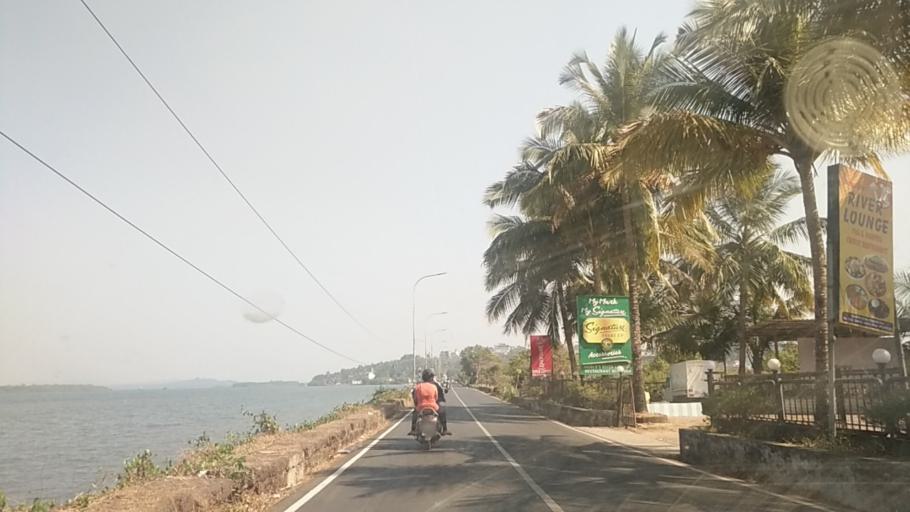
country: IN
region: Goa
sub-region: North Goa
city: Panaji
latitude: 15.5025
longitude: 73.8542
